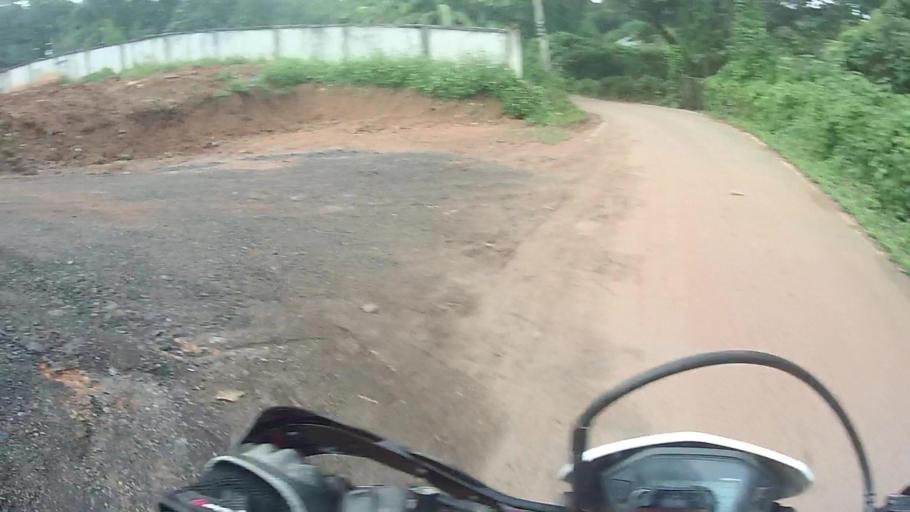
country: TH
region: Chiang Mai
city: Mae Taeng
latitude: 19.0907
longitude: 98.8456
